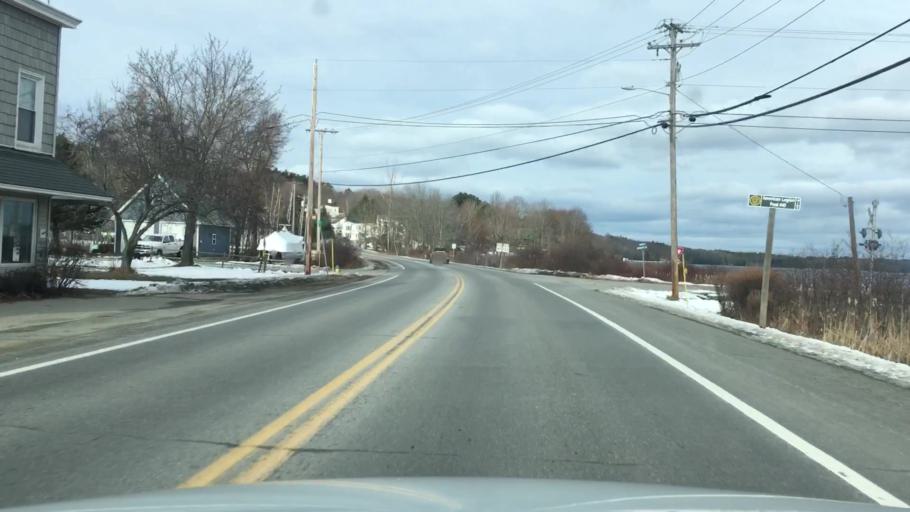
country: US
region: Maine
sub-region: Kennebec County
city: Winthrop
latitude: 44.3088
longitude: -69.9766
